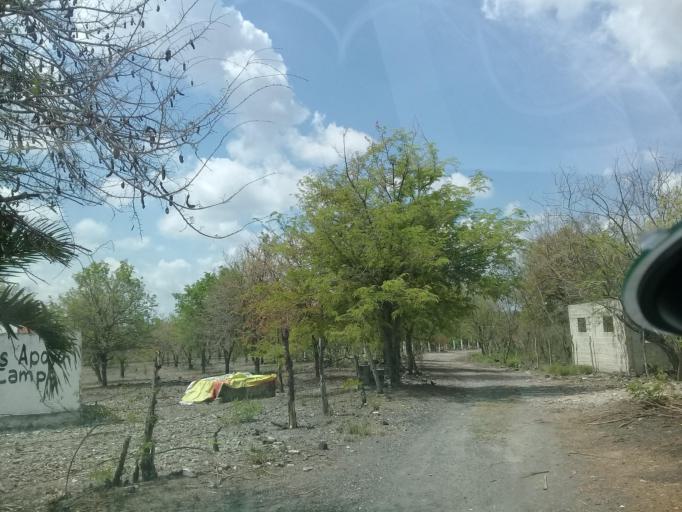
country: MX
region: Veracruz
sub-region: Emiliano Zapata
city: Plan del Rio
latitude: 19.4041
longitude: -96.6459
